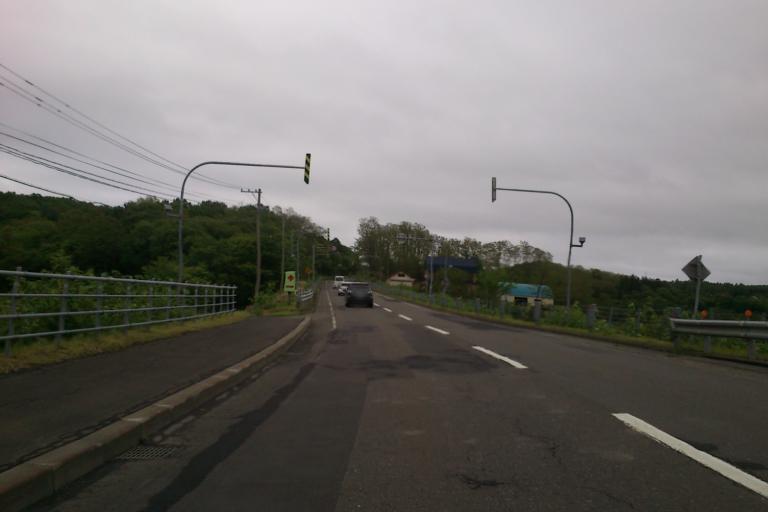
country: JP
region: Hokkaido
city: Ishikari
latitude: 43.3244
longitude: 141.4435
